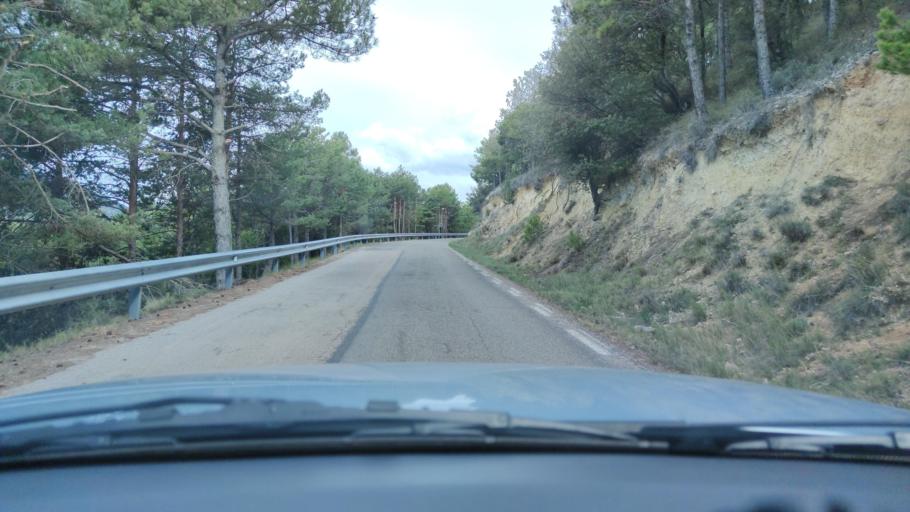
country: ES
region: Catalonia
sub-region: Provincia de Lleida
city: Coll de Nargo
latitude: 42.2490
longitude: 1.3622
